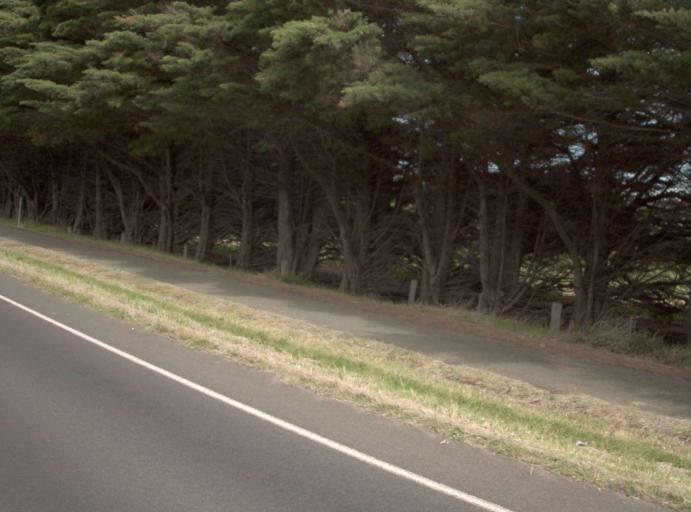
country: AU
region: Victoria
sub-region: Bass Coast
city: Phillip Island
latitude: -38.4821
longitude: 145.2512
